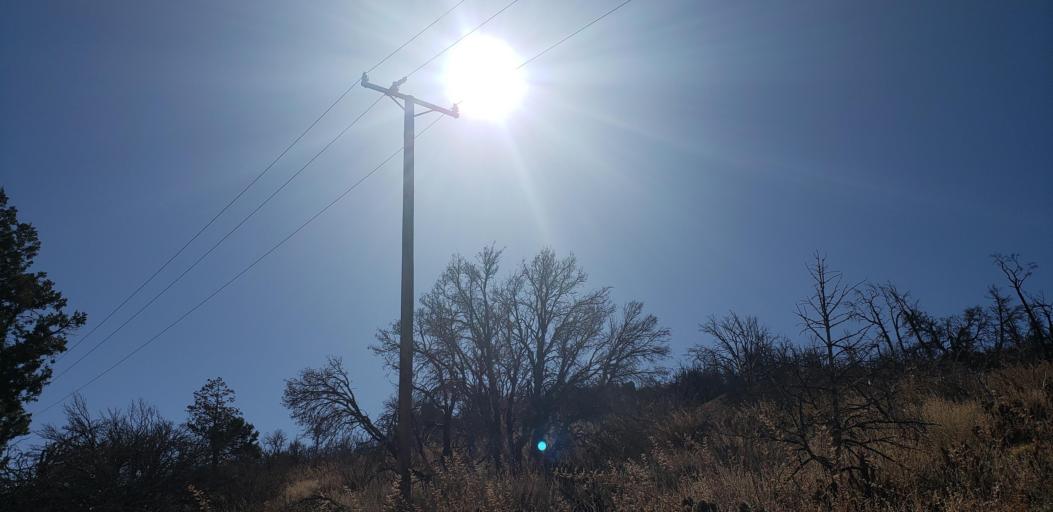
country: US
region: California
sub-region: San Bernardino County
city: Big Bear City
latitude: 34.3042
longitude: -116.8330
